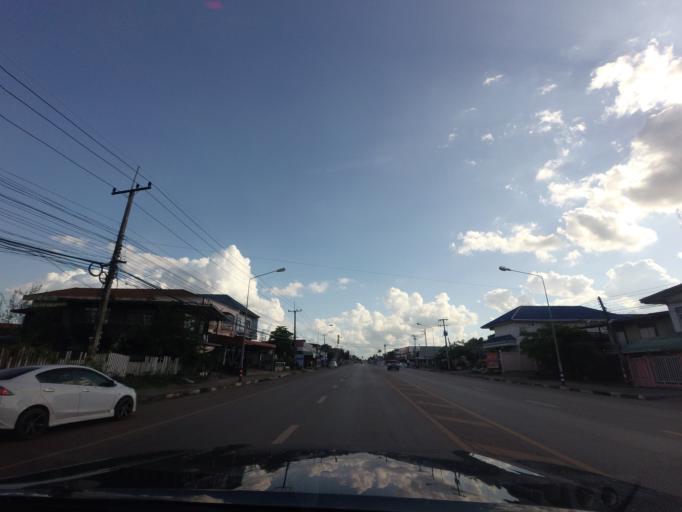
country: TH
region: Changwat Udon Thani
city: Ban Dung
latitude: 17.6894
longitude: 103.2571
